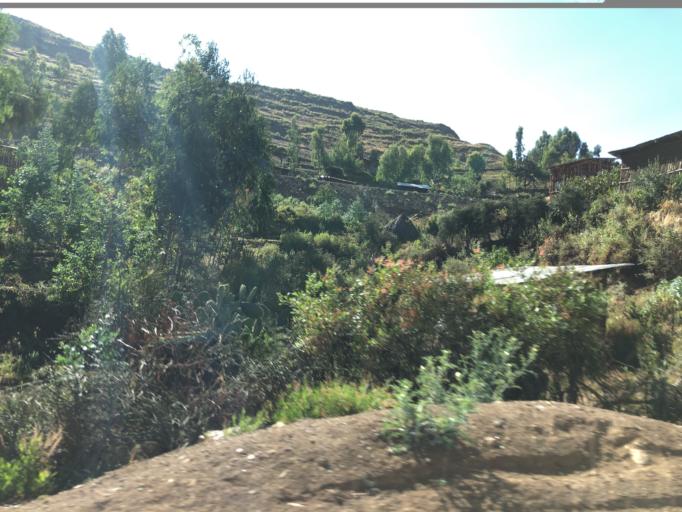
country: ET
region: Amhara
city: Lalibela
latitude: 12.0095
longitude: 39.0517
